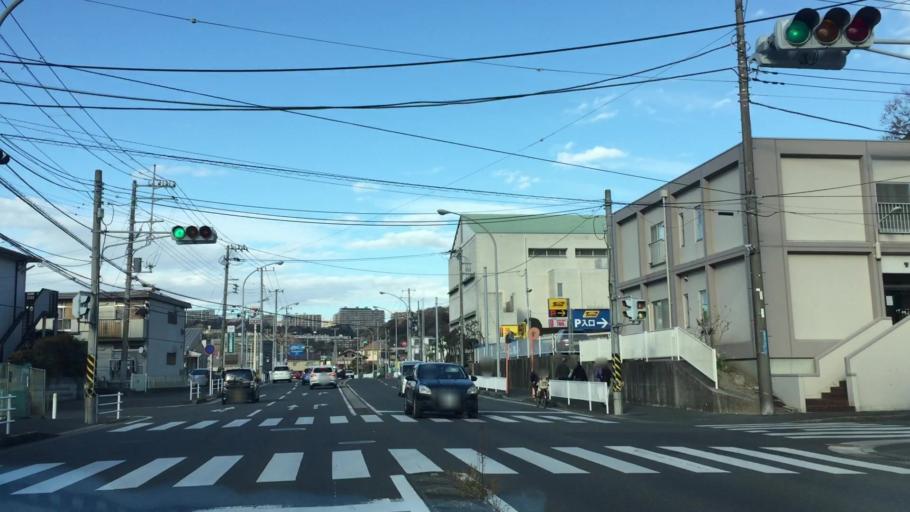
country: JP
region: Kanagawa
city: Zushi
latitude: 35.3412
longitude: 139.6114
